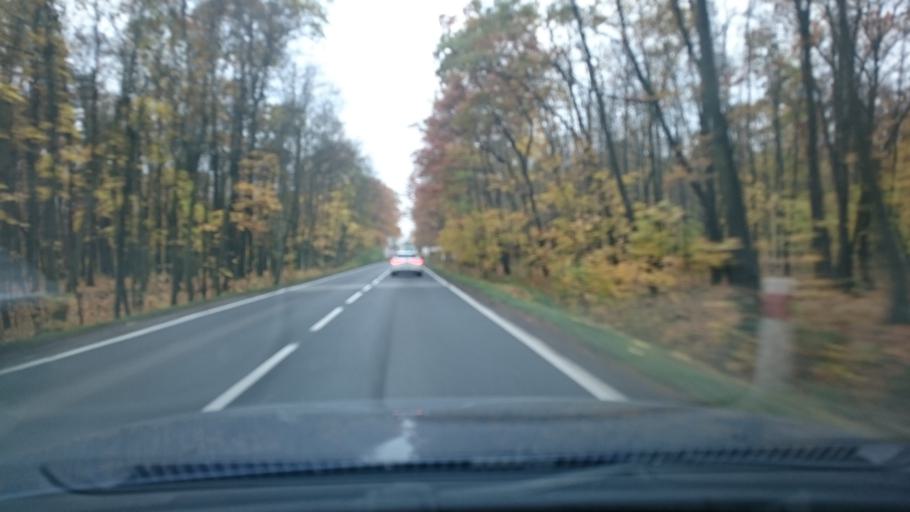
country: PL
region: Silesian Voivodeship
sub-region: Rybnik
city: Rybnik
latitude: 50.1109
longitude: 18.5846
